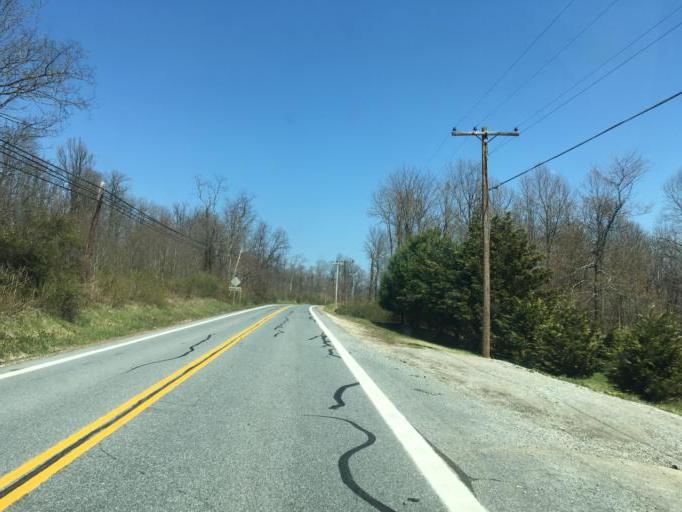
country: US
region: Maryland
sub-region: Washington County
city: Smithsburg
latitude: 39.6369
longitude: -77.5219
